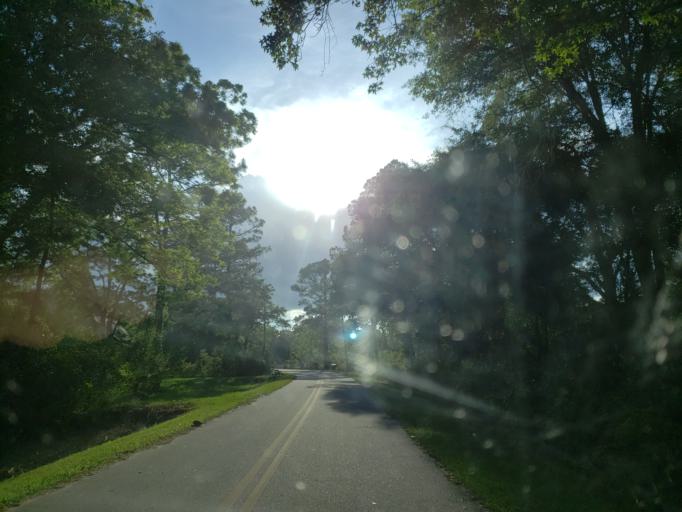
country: US
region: Georgia
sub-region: Lowndes County
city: Hahira
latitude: 31.0451
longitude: -83.3883
